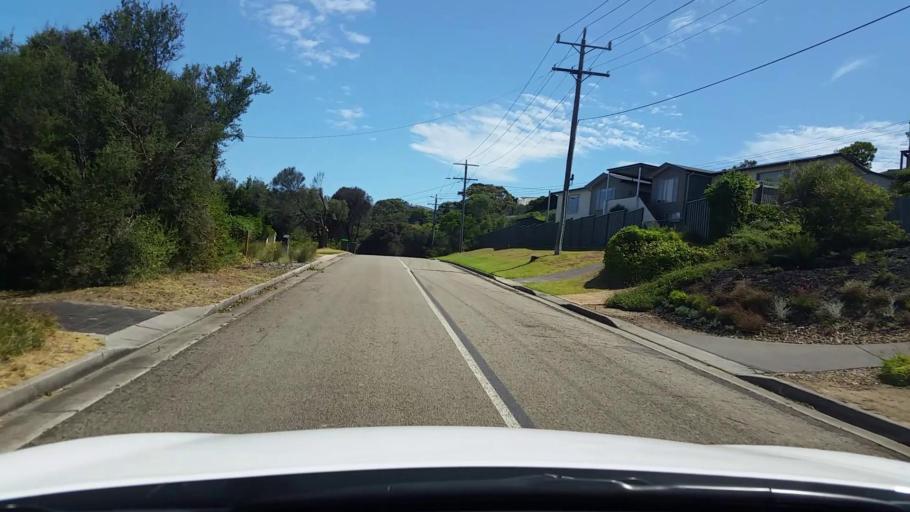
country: AU
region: Victoria
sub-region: Mornington Peninsula
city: Safety Beach
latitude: -38.3013
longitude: 144.9939
